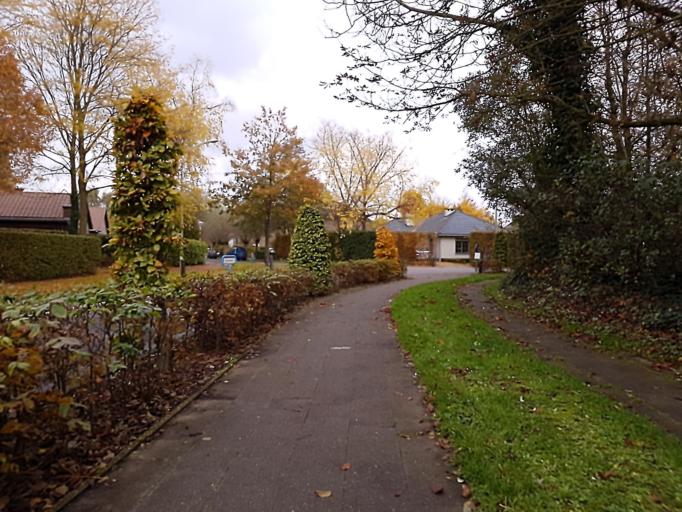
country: BE
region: Flanders
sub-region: Provincie Antwerpen
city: Hove
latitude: 51.1453
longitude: 4.4789
